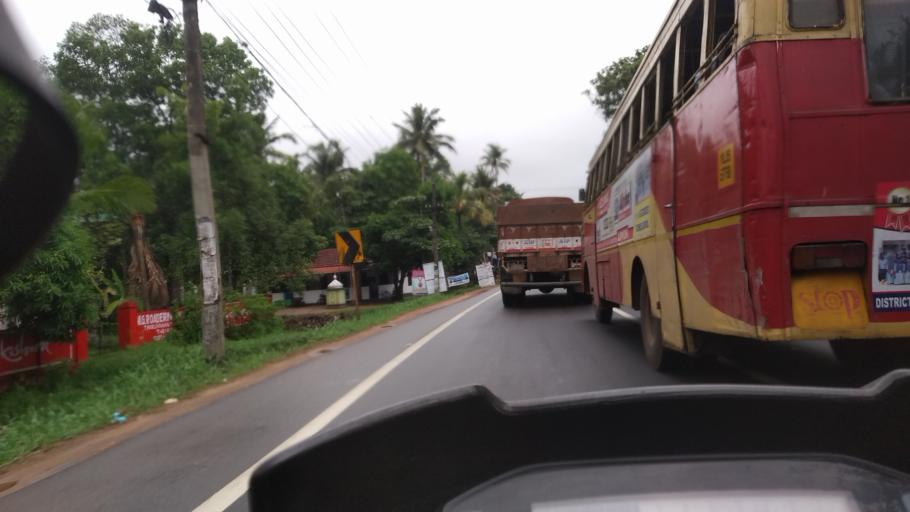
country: IN
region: Kerala
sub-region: Alappuzha
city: Mavelikara
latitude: 9.2929
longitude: 76.4346
